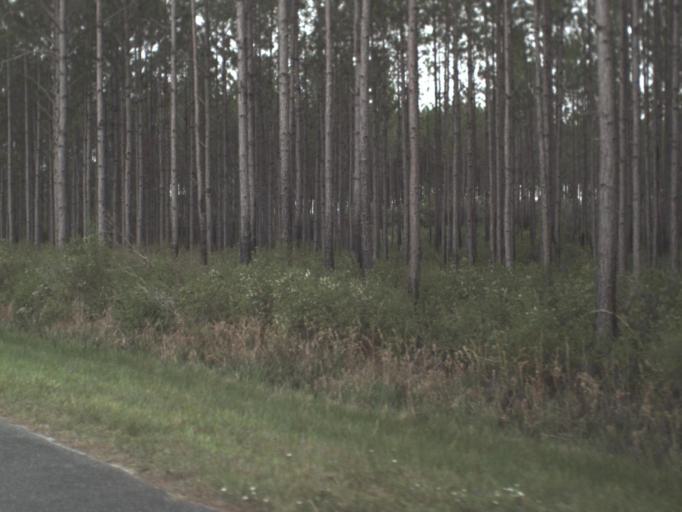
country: US
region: Florida
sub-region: Franklin County
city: Eastpoint
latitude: 29.8025
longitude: -84.8338
